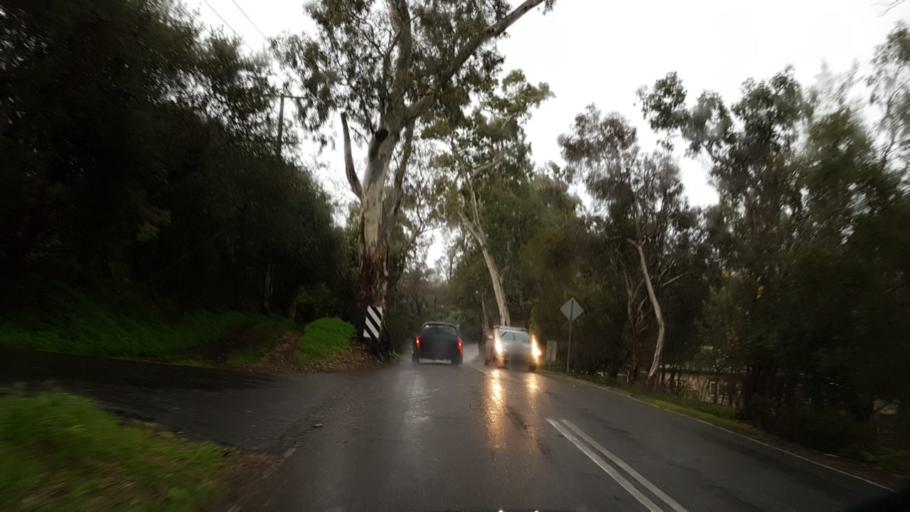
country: AU
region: South Australia
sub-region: Mitcham
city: Blackwood
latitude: -35.0277
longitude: 138.6247
